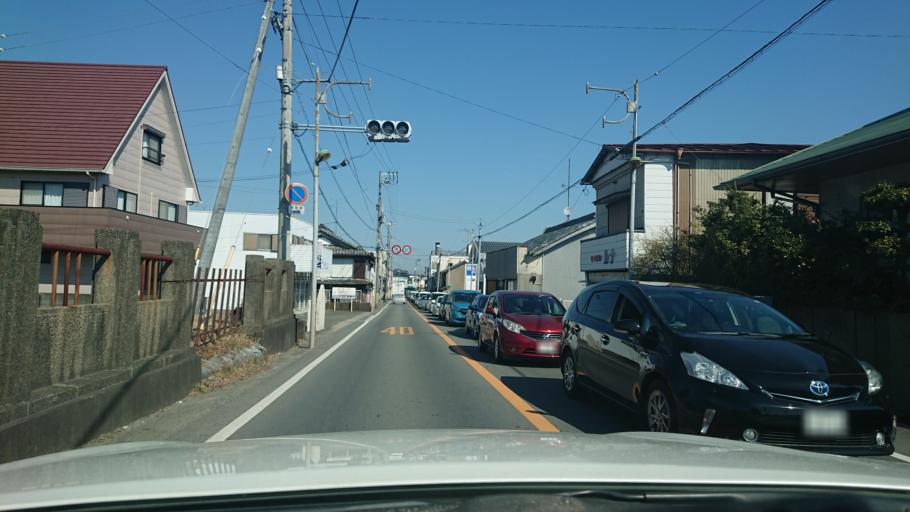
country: JP
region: Tokushima
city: Anan
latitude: 33.9411
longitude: 134.6221
